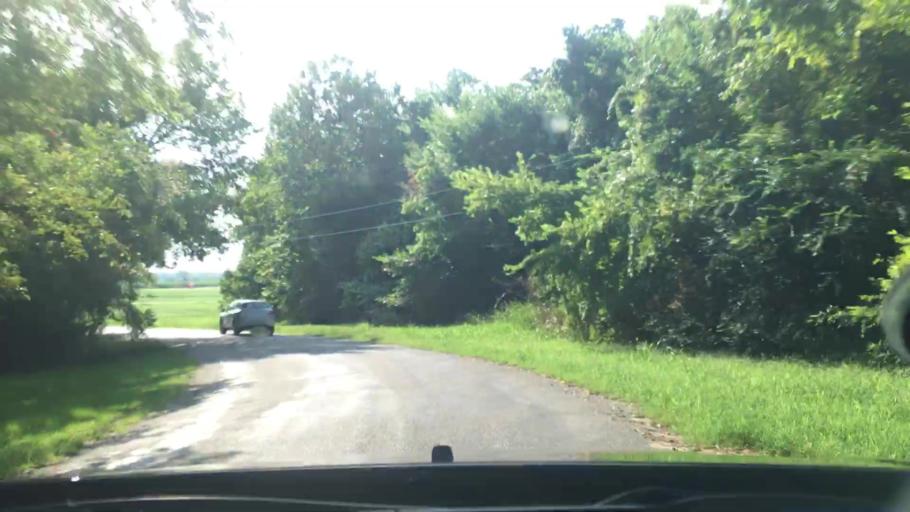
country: US
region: Oklahoma
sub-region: Johnston County
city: Tishomingo
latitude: 34.2160
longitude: -96.6709
